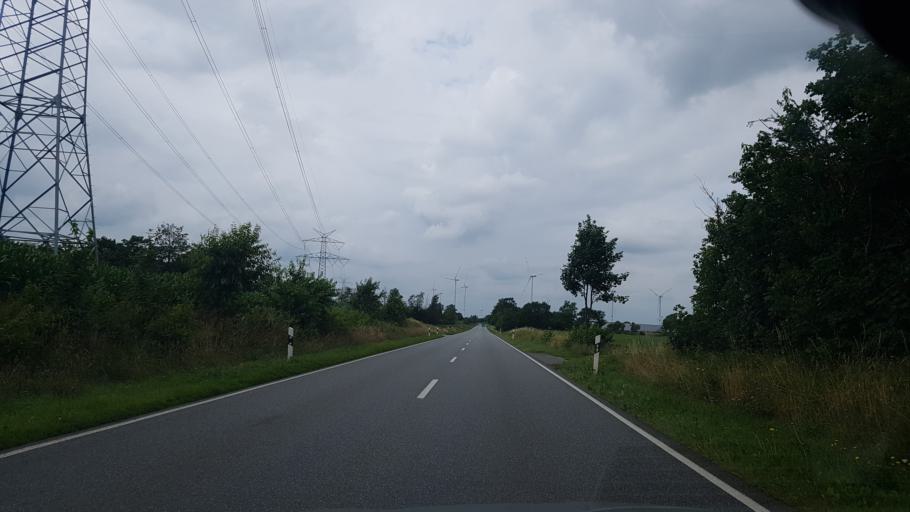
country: DE
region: Schleswig-Holstein
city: Jardelund
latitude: 54.8324
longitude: 9.2154
